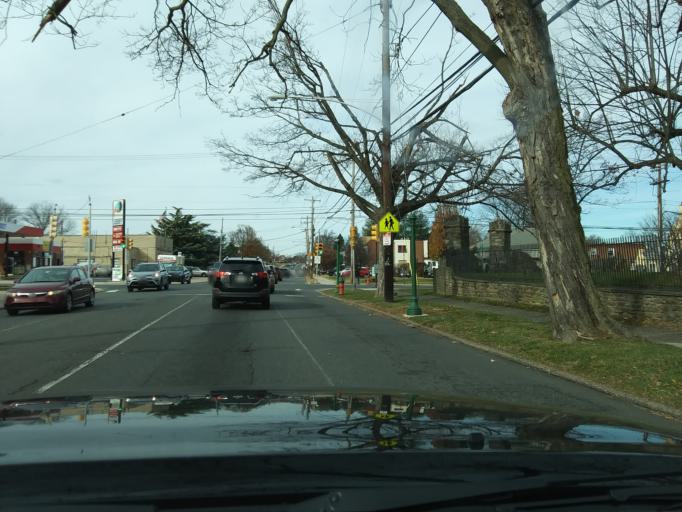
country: US
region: Pennsylvania
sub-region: Montgomery County
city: Rockledge
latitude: 40.0727
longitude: -75.0754
